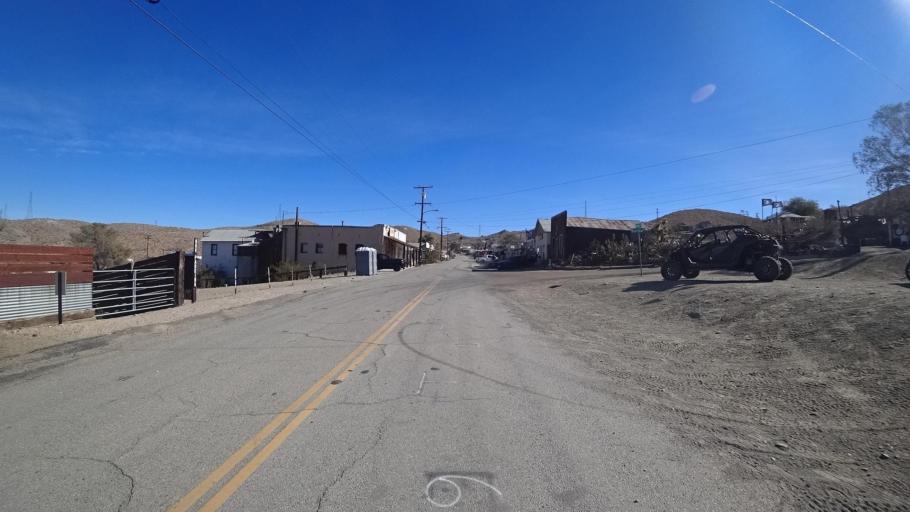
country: US
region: California
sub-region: Kern County
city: Ridgecrest
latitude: 35.3682
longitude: -117.6569
